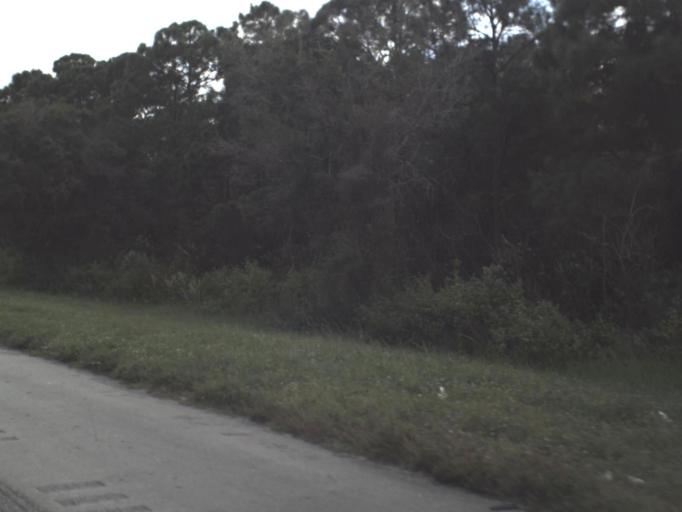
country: US
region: Florida
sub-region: Saint Lucie County
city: Port Saint Lucie
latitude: 27.2409
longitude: -80.3454
